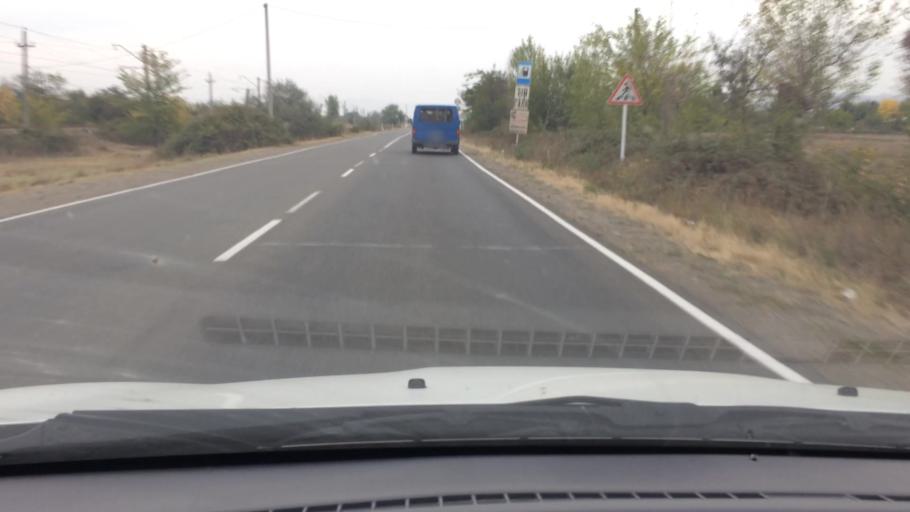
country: GE
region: Kvemo Kartli
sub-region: Marneuli
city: Marneuli
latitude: 41.4423
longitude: 44.8168
